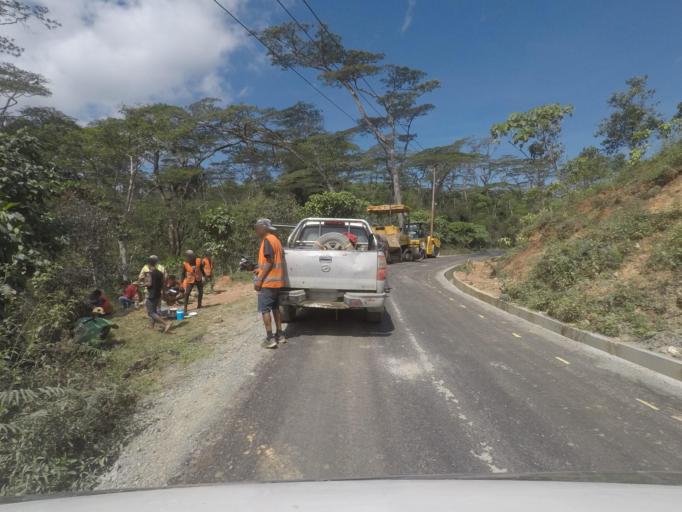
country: TL
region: Ermera
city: Gleno
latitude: -8.7495
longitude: 125.3409
